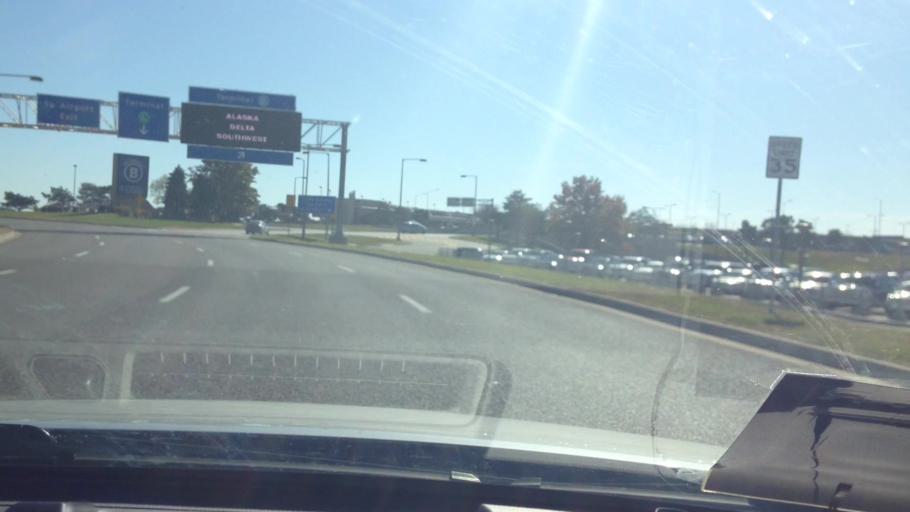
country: US
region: Missouri
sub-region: Platte County
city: Weatherby Lake
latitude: 39.2975
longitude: -94.7181
